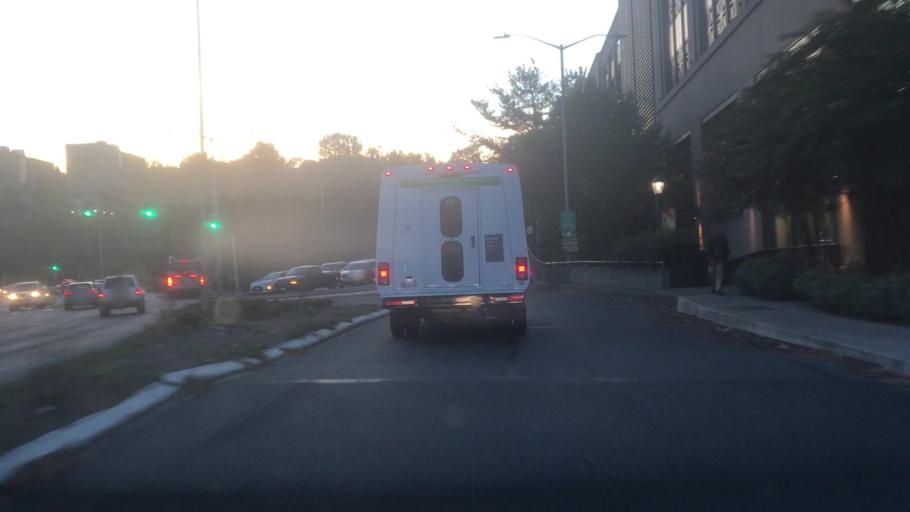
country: US
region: Washington
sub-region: King County
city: Seattle
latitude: 47.6613
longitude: -122.2979
